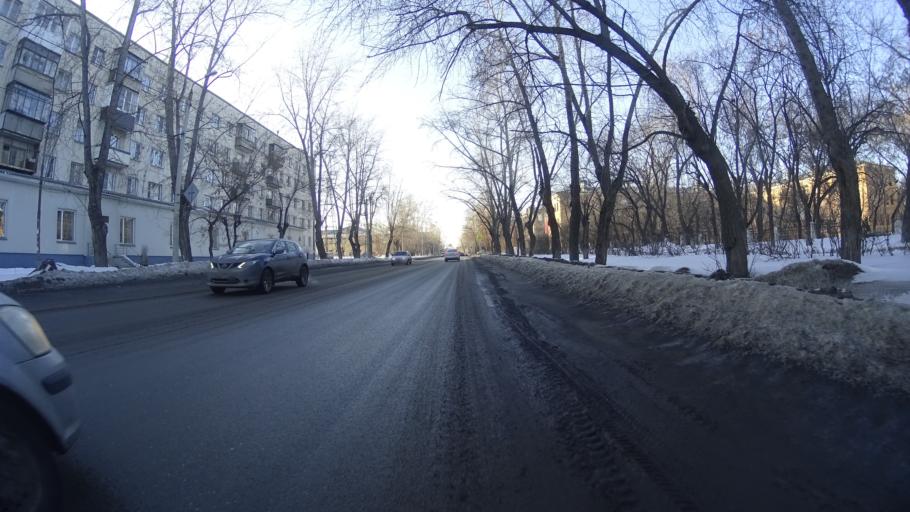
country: RU
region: Chelyabinsk
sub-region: Gorod Chelyabinsk
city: Chelyabinsk
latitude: 55.1288
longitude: 61.4675
